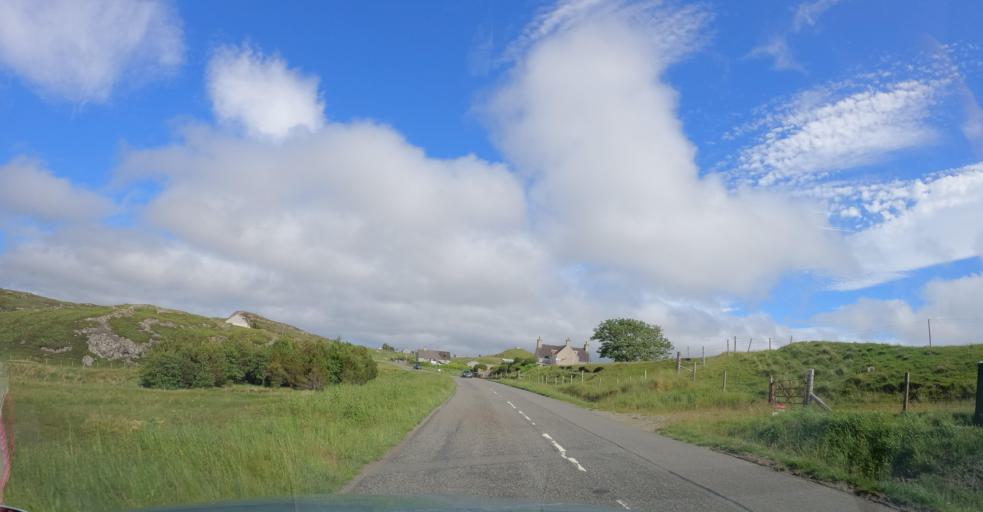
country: GB
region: Scotland
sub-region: Eilean Siar
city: Stornoway
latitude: 58.1057
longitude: -6.5385
